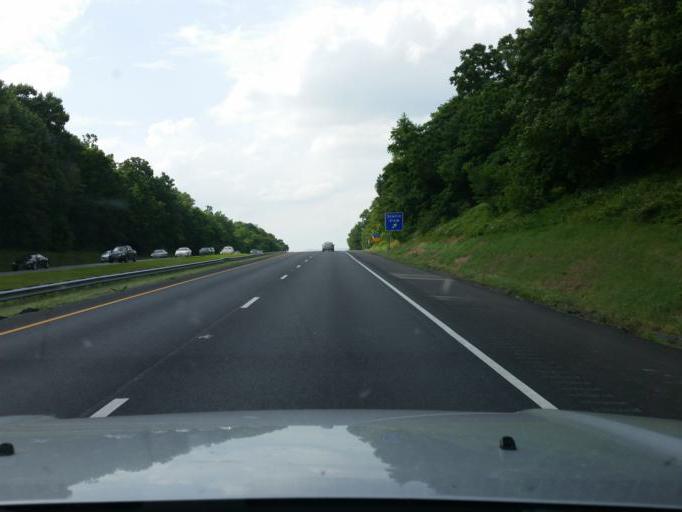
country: US
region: Maryland
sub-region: Frederick County
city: Urbana
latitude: 39.3435
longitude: -77.3864
